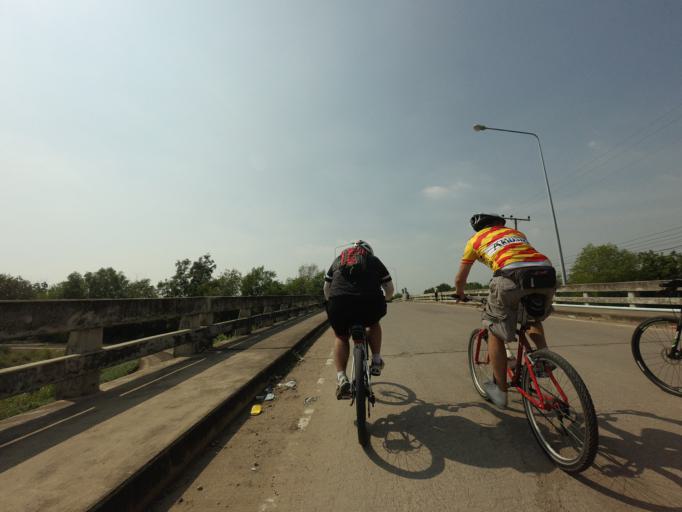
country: TH
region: Samut Sakhon
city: Samut Sakhon
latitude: 13.5131
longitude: 100.3871
